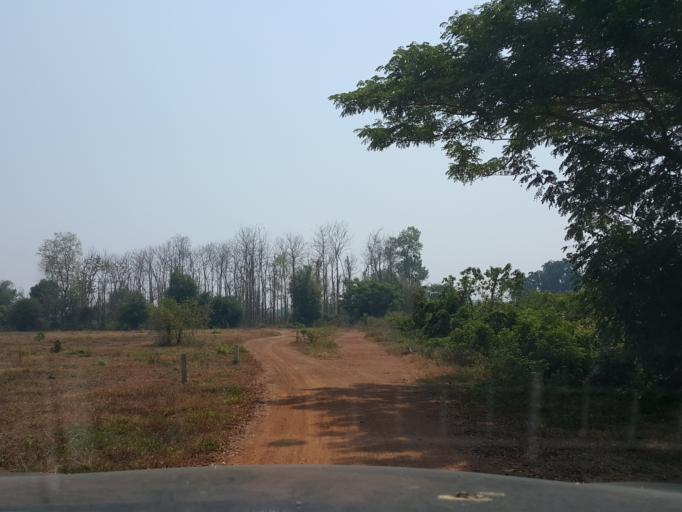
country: TH
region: Sukhothai
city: Thung Saliam
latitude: 17.3150
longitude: 99.5631
